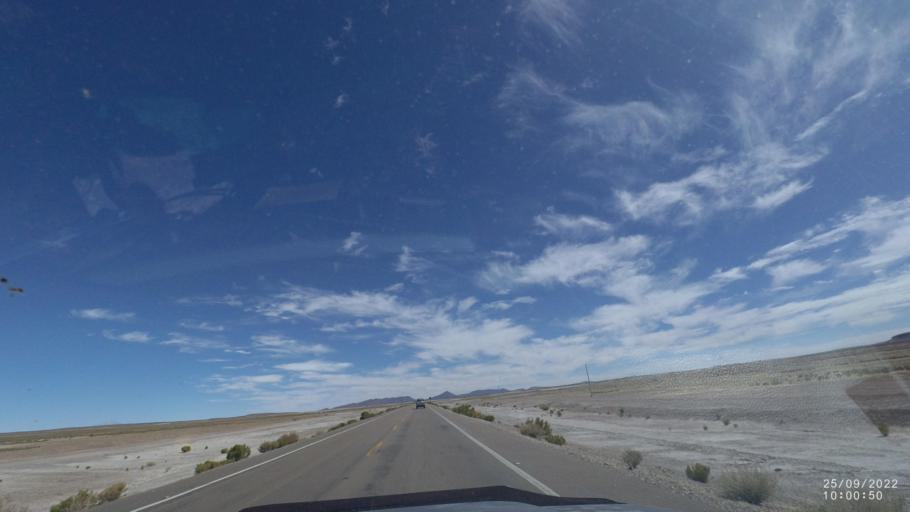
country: BO
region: Potosi
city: Colchani
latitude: -20.2668
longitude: -66.9509
